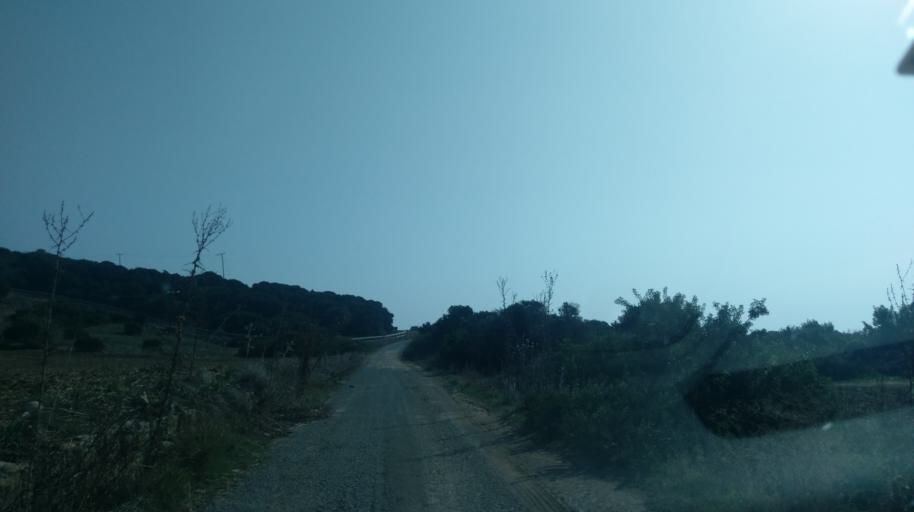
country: CY
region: Ammochostos
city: Rizokarpaso
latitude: 35.6471
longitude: 34.5530
